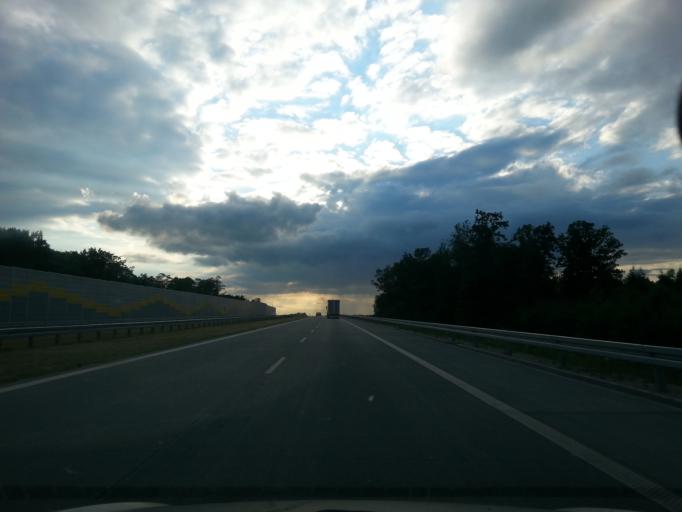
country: PL
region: Lodz Voivodeship
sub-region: Powiat zdunskowolski
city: Zdunska Wola
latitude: 51.5652
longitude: 18.9875
